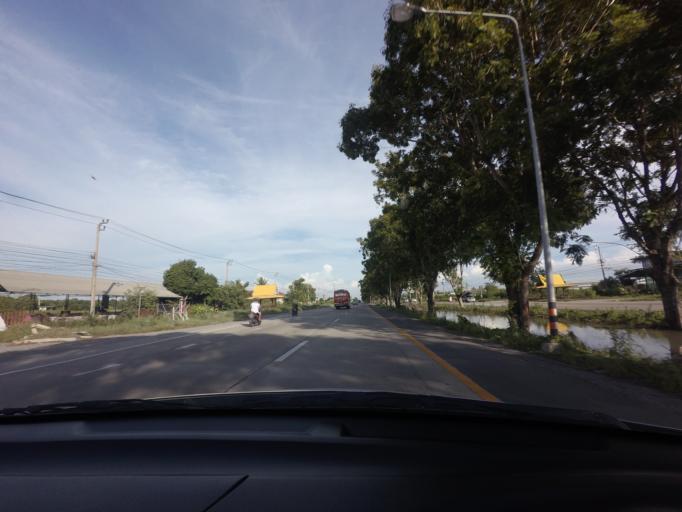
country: TH
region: Pathum Thani
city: Lat Lum Kaeo
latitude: 14.0657
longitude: 100.3258
